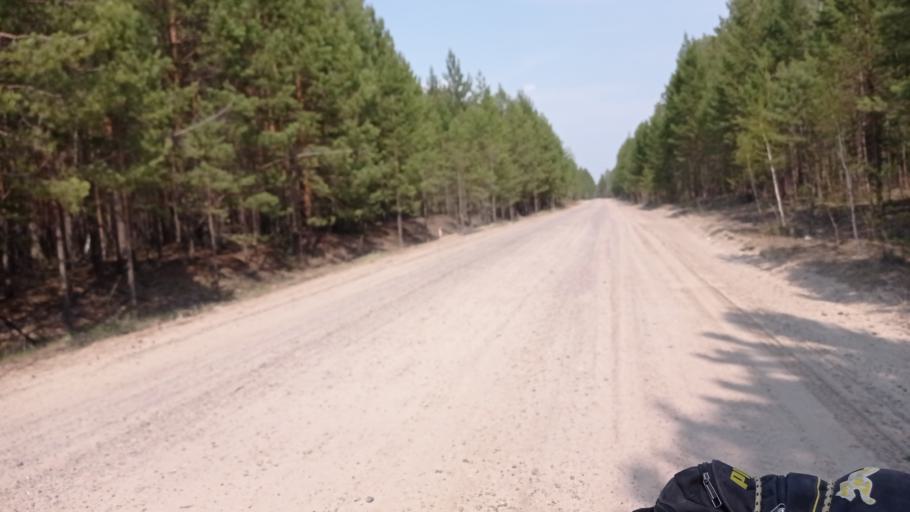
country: RU
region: Tomsk
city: Timiryazevskoye
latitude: 56.4180
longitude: 84.6726
